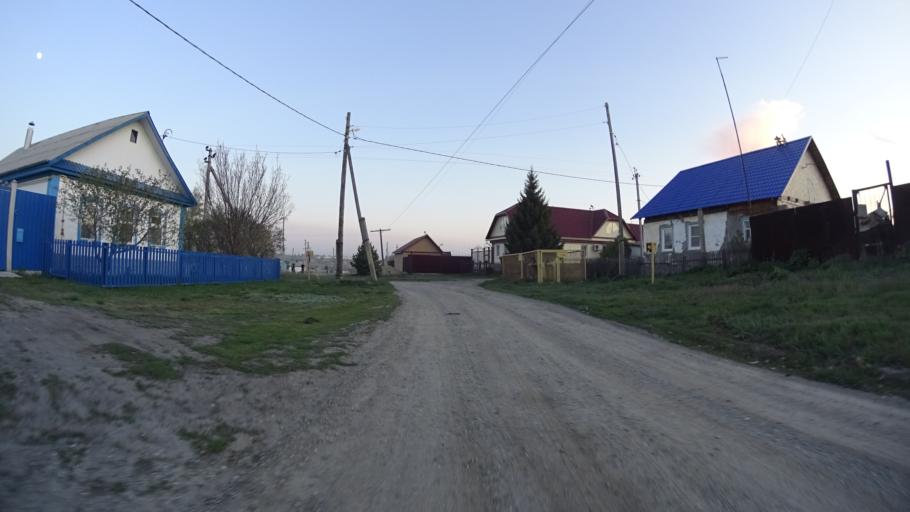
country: RU
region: Chelyabinsk
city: Bobrovka
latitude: 54.0433
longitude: 61.7445
